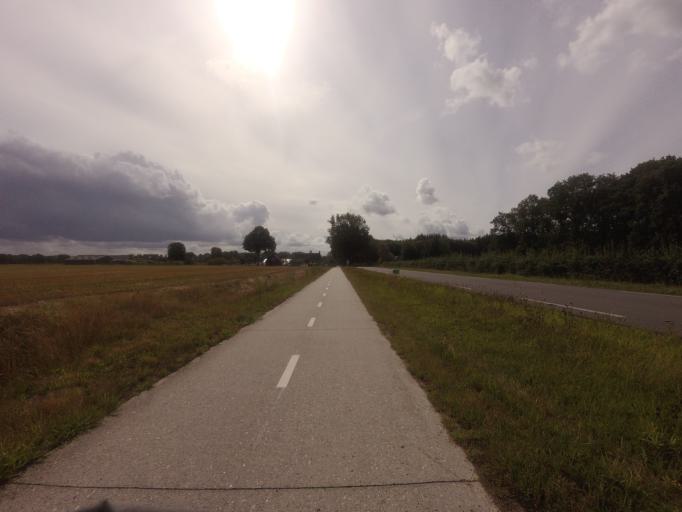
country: NL
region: Drenthe
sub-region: Gemeente Assen
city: Assen
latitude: 53.0515
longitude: 6.4561
